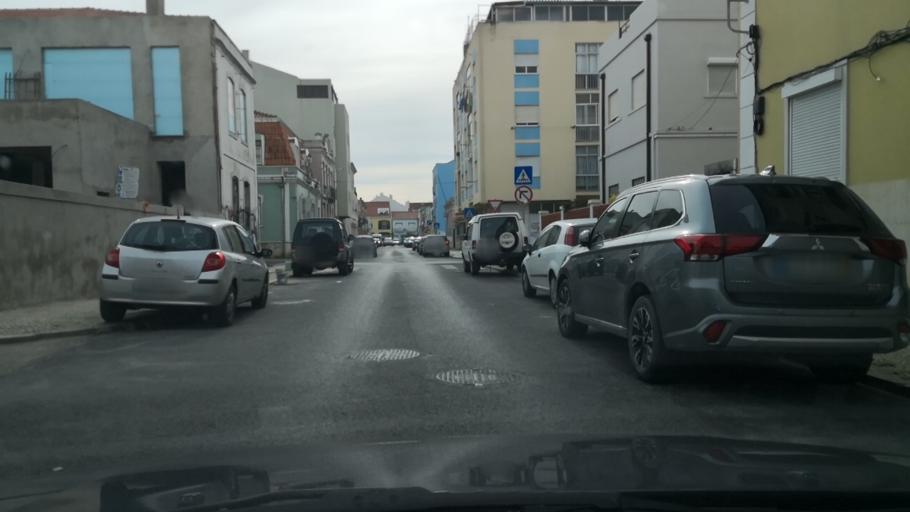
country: PT
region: Setubal
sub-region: Setubal
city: Setubal
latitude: 38.5280
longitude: -8.8874
